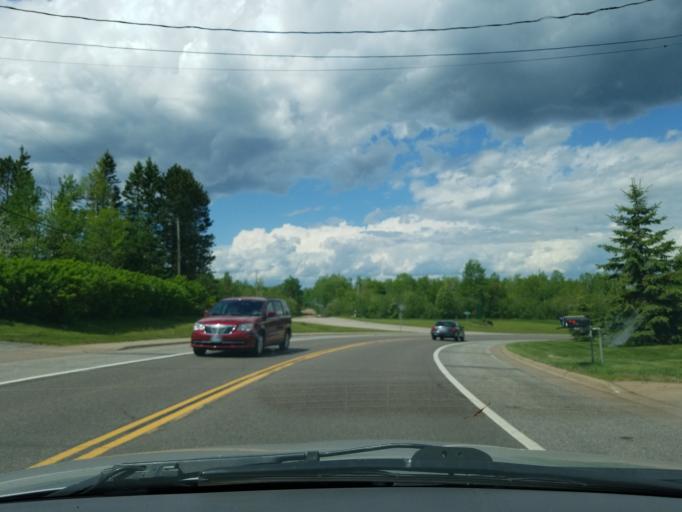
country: US
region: Minnesota
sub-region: Saint Louis County
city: Proctor
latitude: 46.7613
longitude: -92.2221
